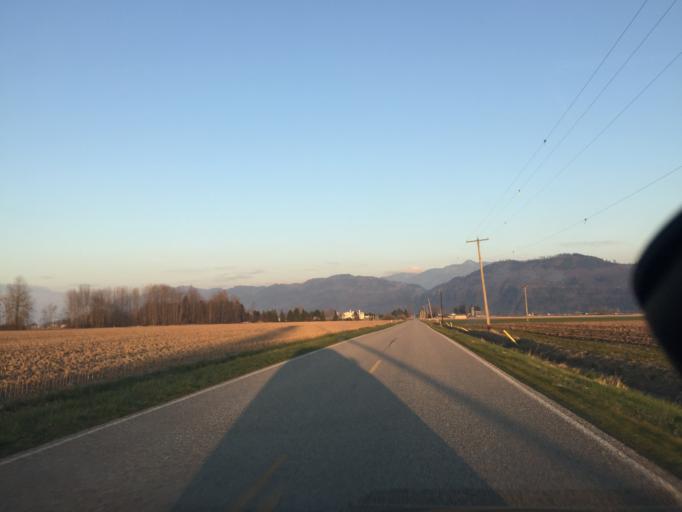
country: US
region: Washington
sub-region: Whatcom County
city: Sumas
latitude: 49.0000
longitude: -122.2326
